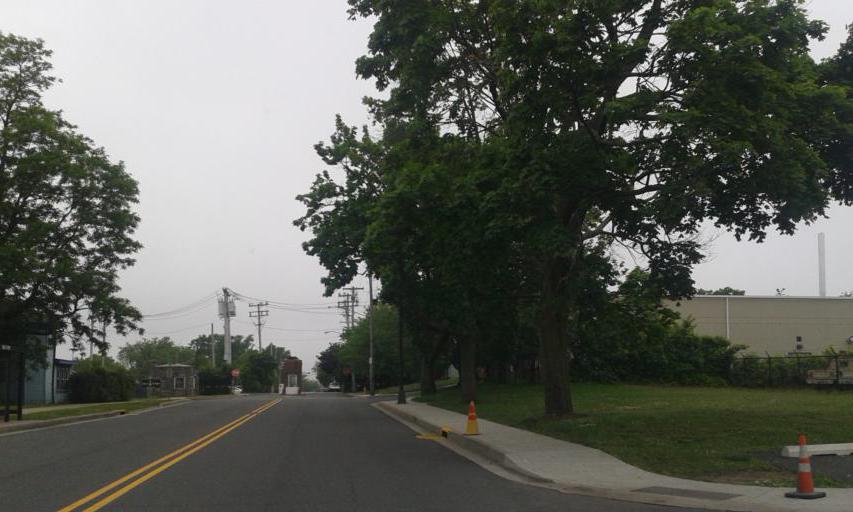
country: US
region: New York
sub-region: Kings County
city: Bensonhurst
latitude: 40.6002
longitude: -74.0599
